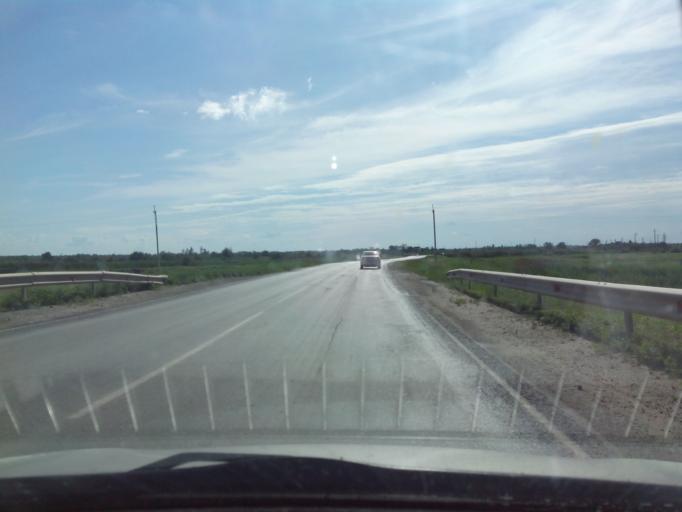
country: RU
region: Astrakhan
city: Kapustin Yar
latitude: 48.5625
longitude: 45.7778
